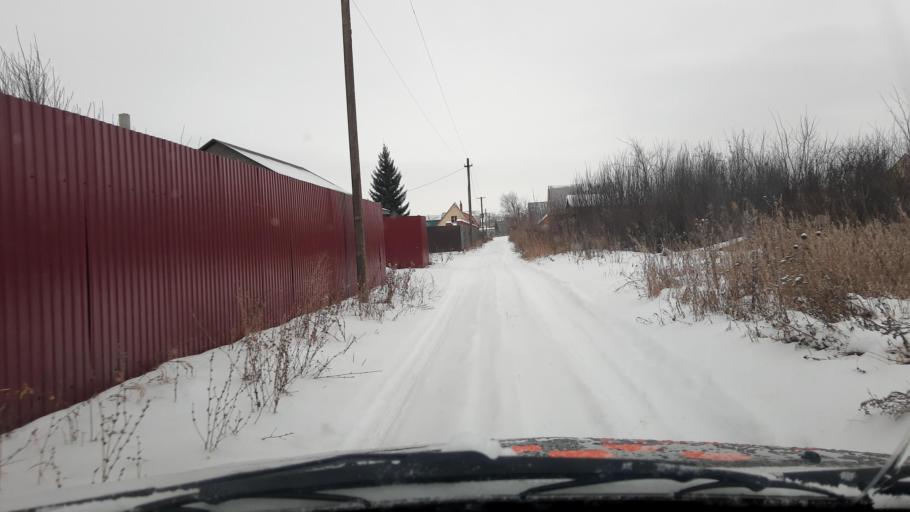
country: RU
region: Bashkortostan
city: Avdon
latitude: 54.4920
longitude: 55.8441
